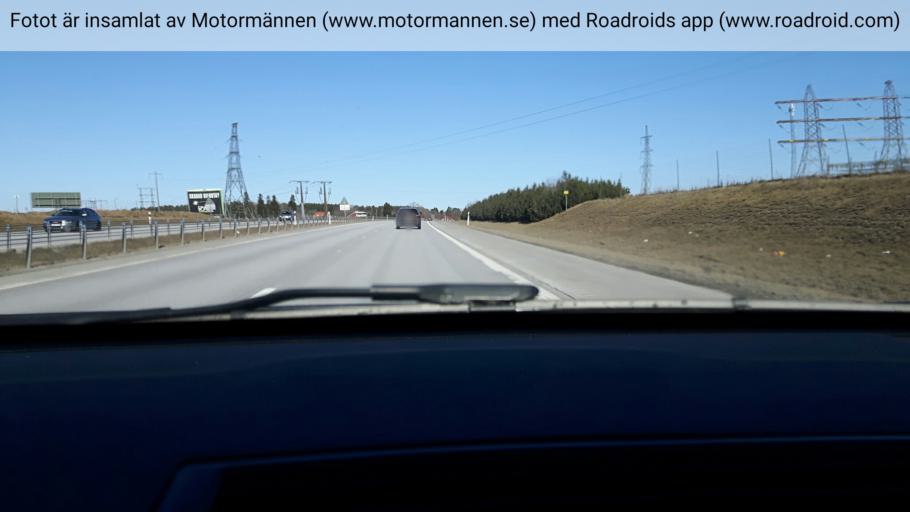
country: SE
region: Uppsala
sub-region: Uppsala Kommun
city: Gamla Uppsala
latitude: 59.9122
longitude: 17.6507
